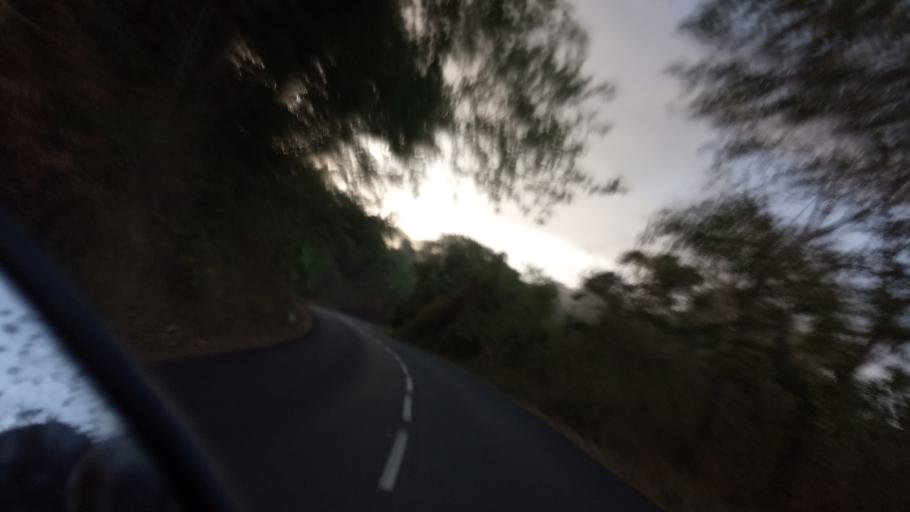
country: YT
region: Kani-Keli
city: Kani Keli
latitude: -12.9276
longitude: 45.1147
